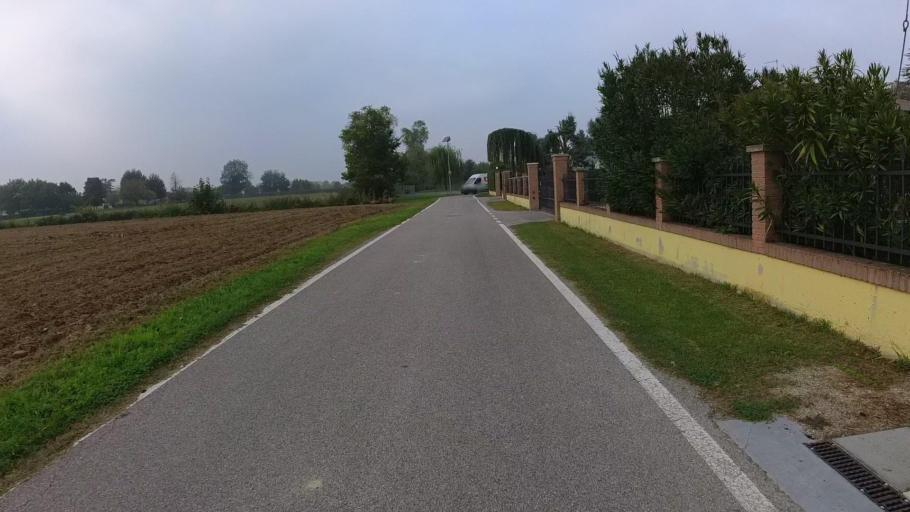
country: IT
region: Veneto
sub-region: Provincia di Venezia
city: Fosso
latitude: 45.3897
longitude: 12.0370
